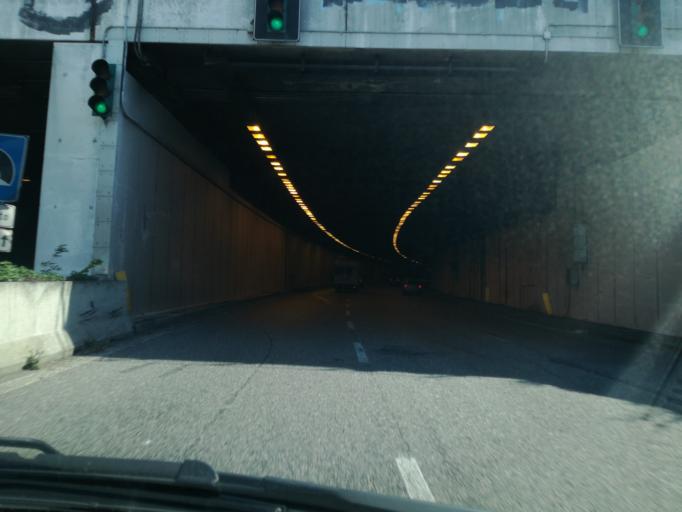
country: IT
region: Lombardy
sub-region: Provincia di Bergamo
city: Ghiaie
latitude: 45.6833
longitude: 9.5724
